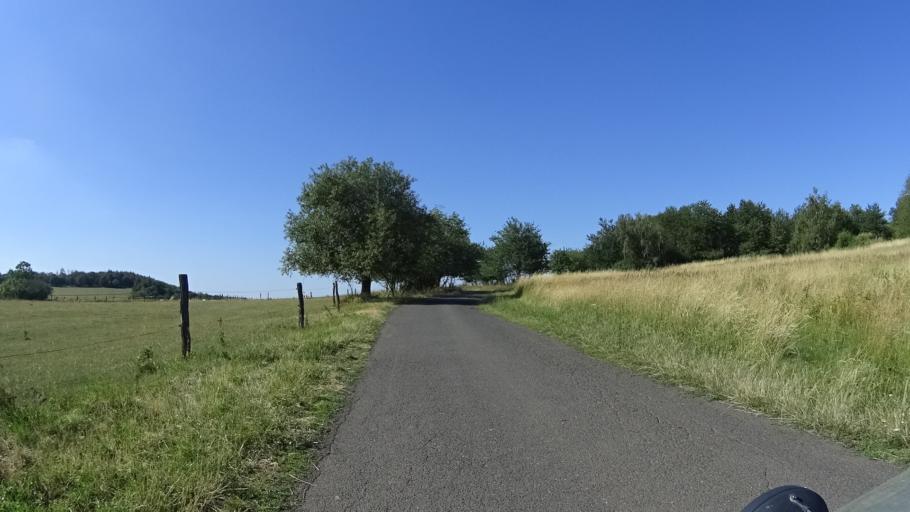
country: CZ
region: Ustecky
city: Zitenice
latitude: 50.5899
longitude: 14.1227
